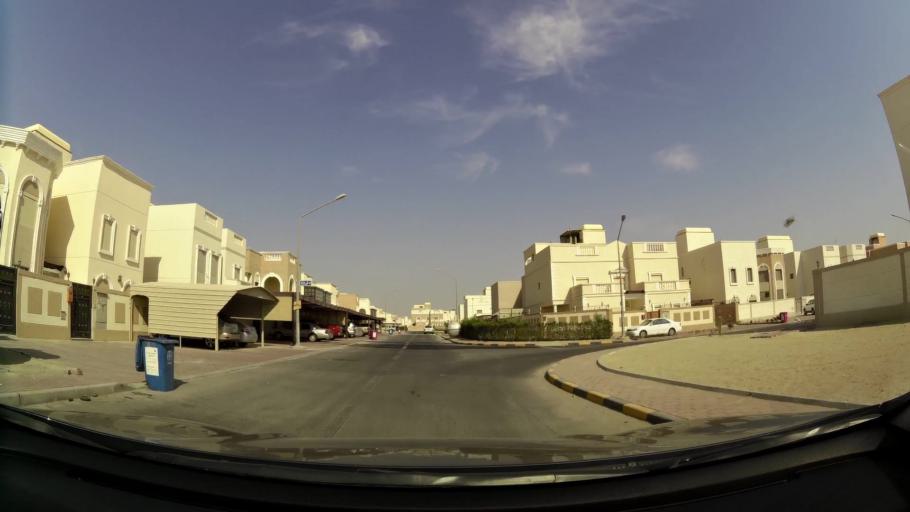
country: KW
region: Al Ahmadi
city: Al Wafrah
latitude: 28.7927
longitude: 48.0670
